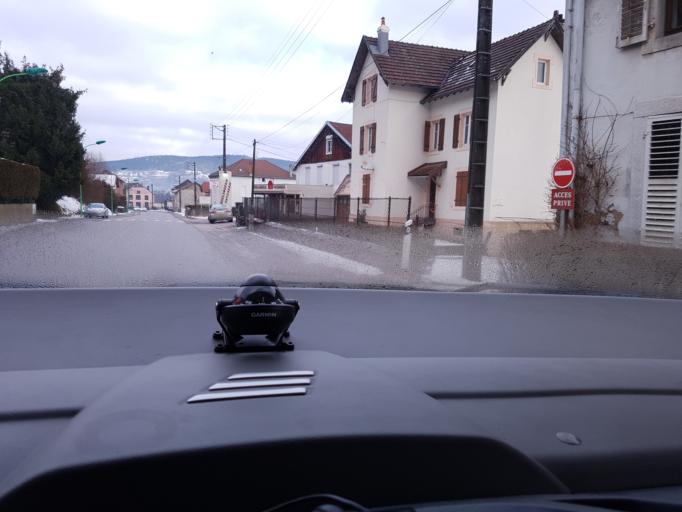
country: FR
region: Lorraine
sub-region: Departement des Vosges
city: Plainfaing
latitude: 48.1783
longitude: 7.0085
